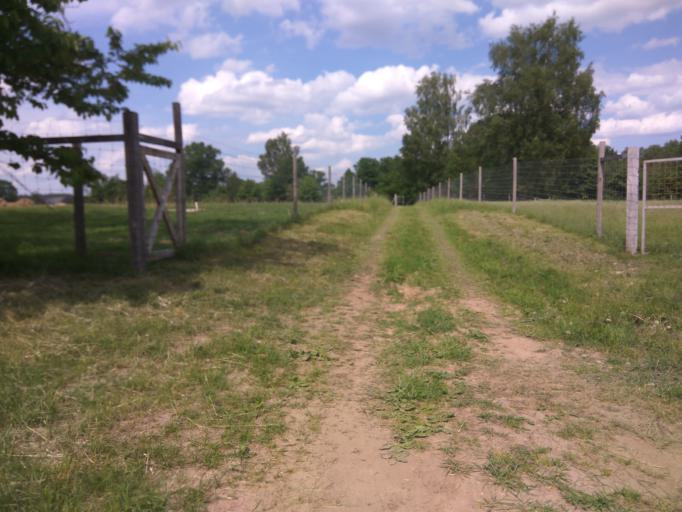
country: LV
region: Kuldigas Rajons
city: Kuldiga
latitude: 56.8890
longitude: 21.9299
